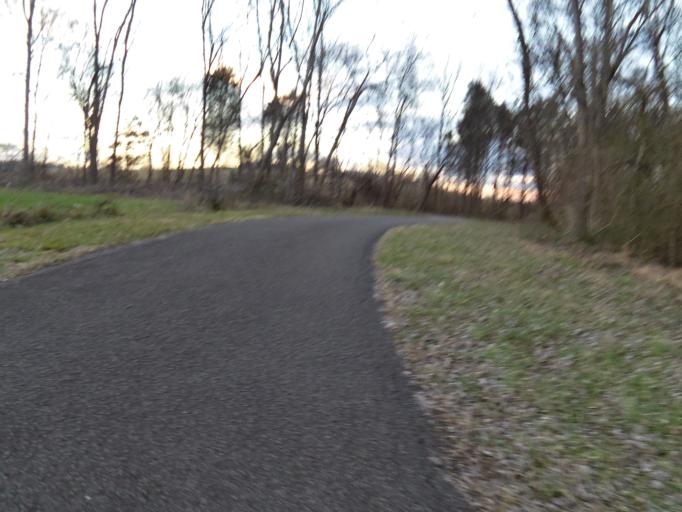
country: US
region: Tennessee
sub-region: Knox County
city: Knoxville
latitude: 35.9538
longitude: -83.8570
